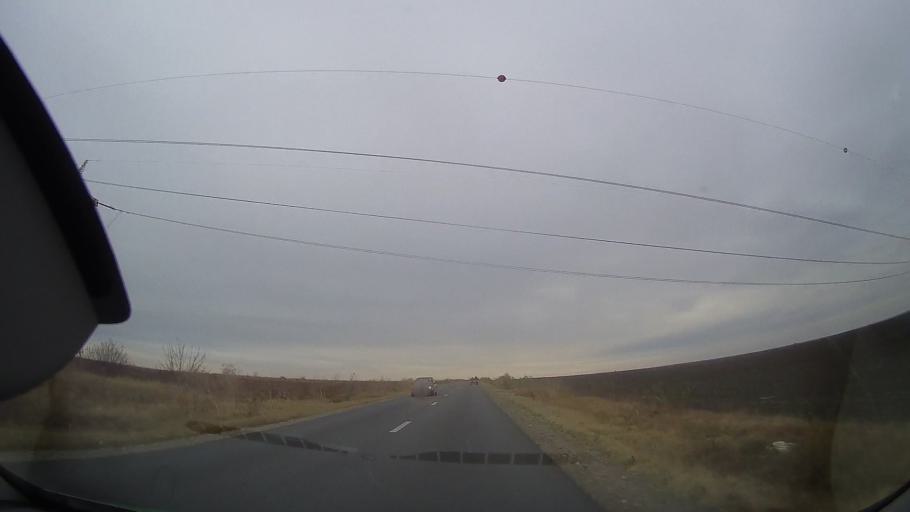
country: RO
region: Ialomita
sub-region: Oras Amara
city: Amara
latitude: 44.6403
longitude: 27.3007
